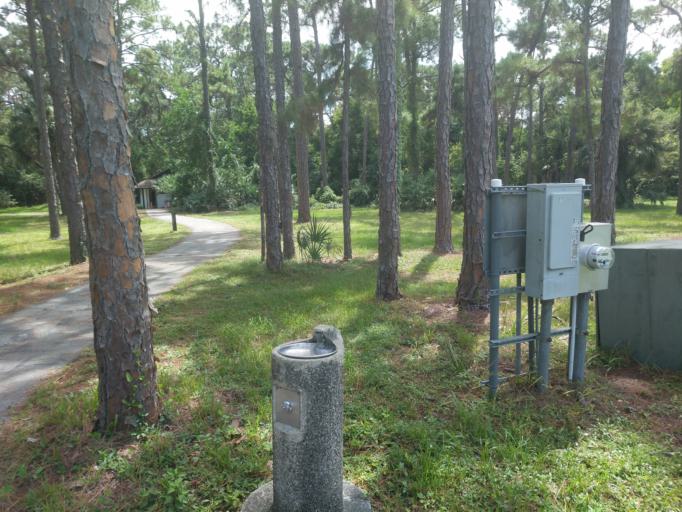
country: US
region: Florida
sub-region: Palm Beach County
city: Kings Point
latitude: 26.4264
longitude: -80.1564
